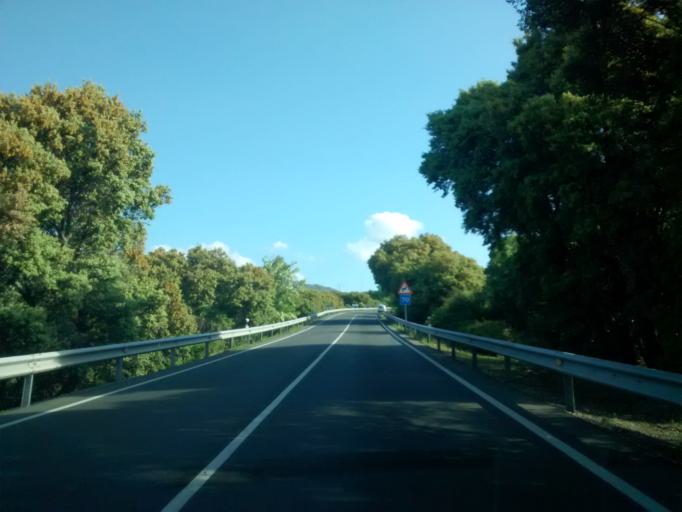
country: ES
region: Madrid
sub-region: Provincia de Madrid
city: Alpedrete
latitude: 40.6710
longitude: -4.0109
